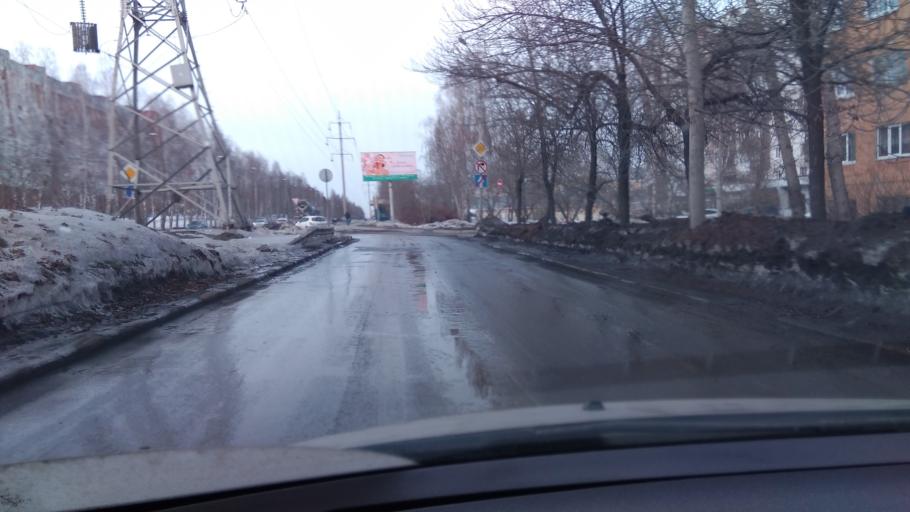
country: RU
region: Sverdlovsk
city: Sovkhoznyy
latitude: 56.7772
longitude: 60.5990
